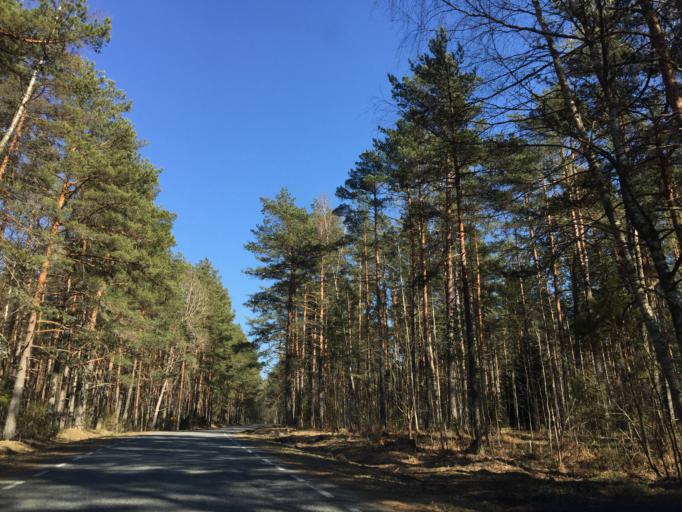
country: EE
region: Ida-Virumaa
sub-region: Johvi vald
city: Johvi
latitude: 59.0033
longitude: 27.3496
